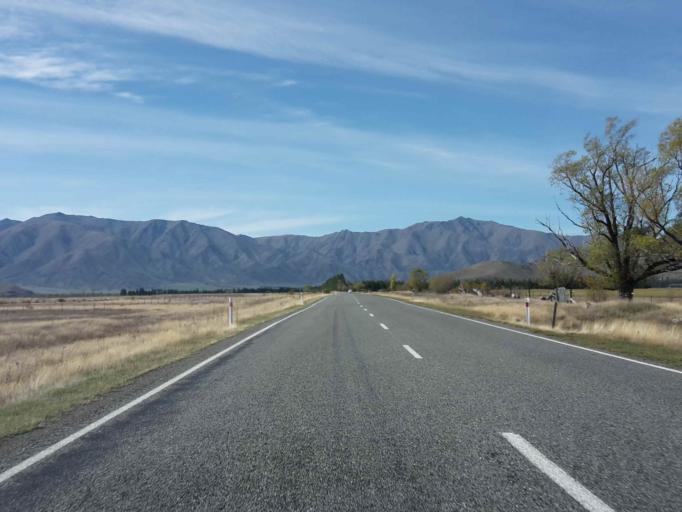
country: NZ
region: Otago
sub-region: Queenstown-Lakes District
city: Wanaka
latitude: -44.4967
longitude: 169.9138
